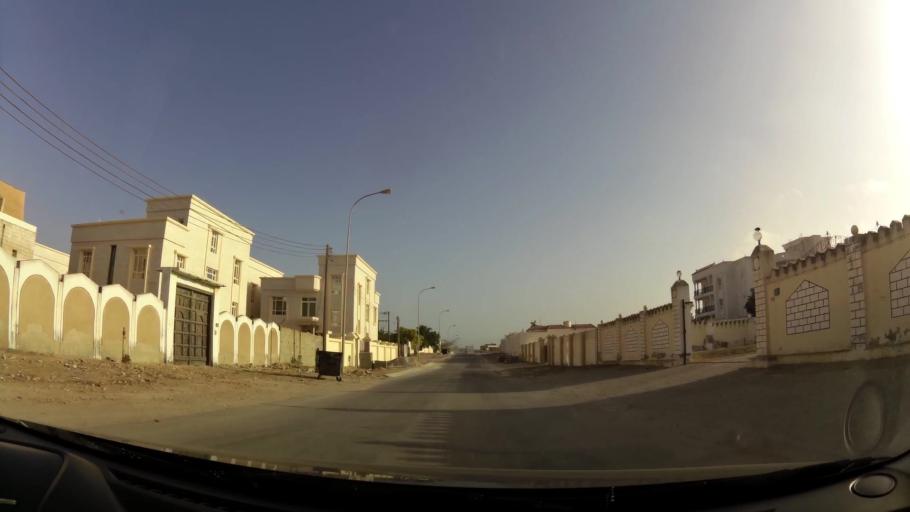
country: OM
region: Zufar
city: Salalah
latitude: 17.0065
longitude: 54.0312
